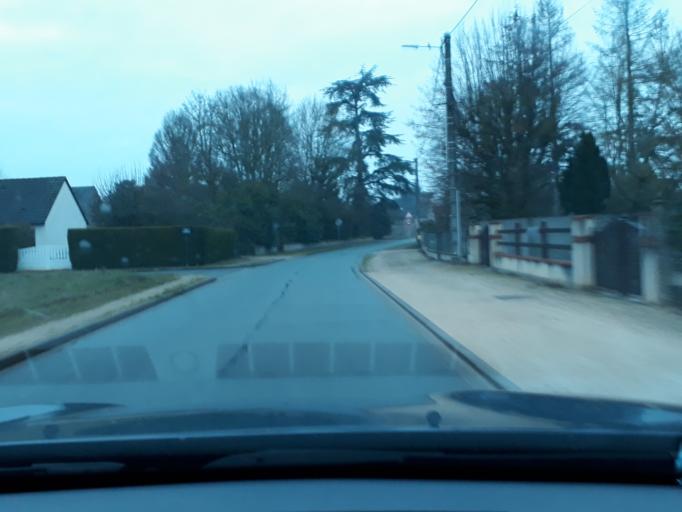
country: FR
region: Centre
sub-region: Departement du Loiret
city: Loury
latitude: 47.9982
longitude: 2.0841
